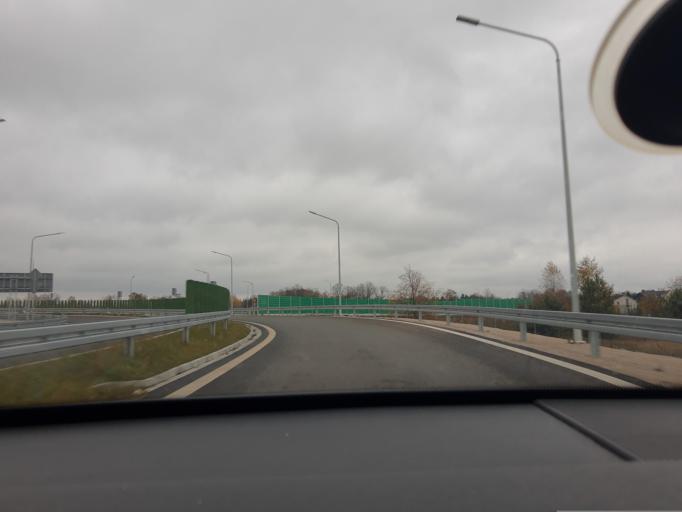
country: PL
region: Lodz Voivodeship
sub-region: Powiat pabianicki
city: Konstantynow Lodzki
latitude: 51.7284
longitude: 19.3546
